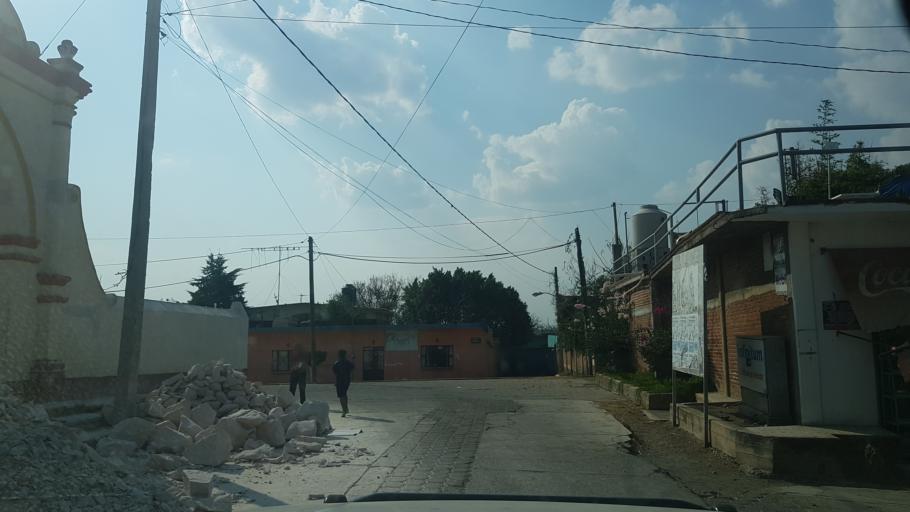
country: MX
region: Morelos
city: Tlacotepec
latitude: 18.7831
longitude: -98.7211
